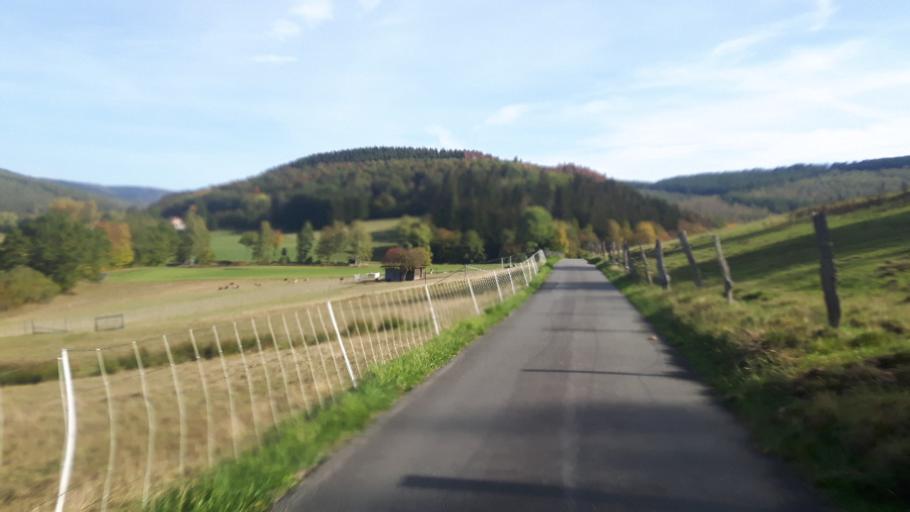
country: DE
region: North Rhine-Westphalia
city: Netphen
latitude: 50.8866
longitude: 8.1839
